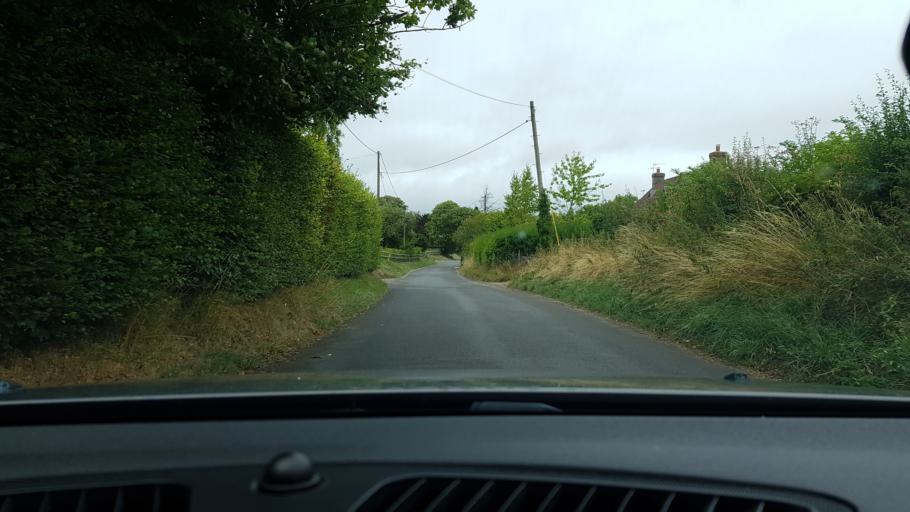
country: GB
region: England
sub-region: Wiltshire
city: Shalbourne
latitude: 51.3601
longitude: -1.5246
